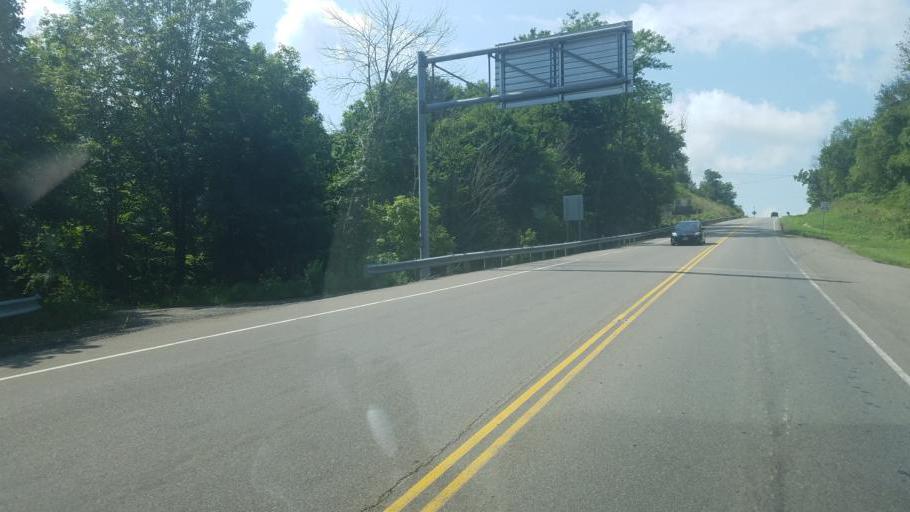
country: US
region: Ohio
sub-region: Licking County
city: Granville
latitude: 40.0574
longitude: -82.5211
